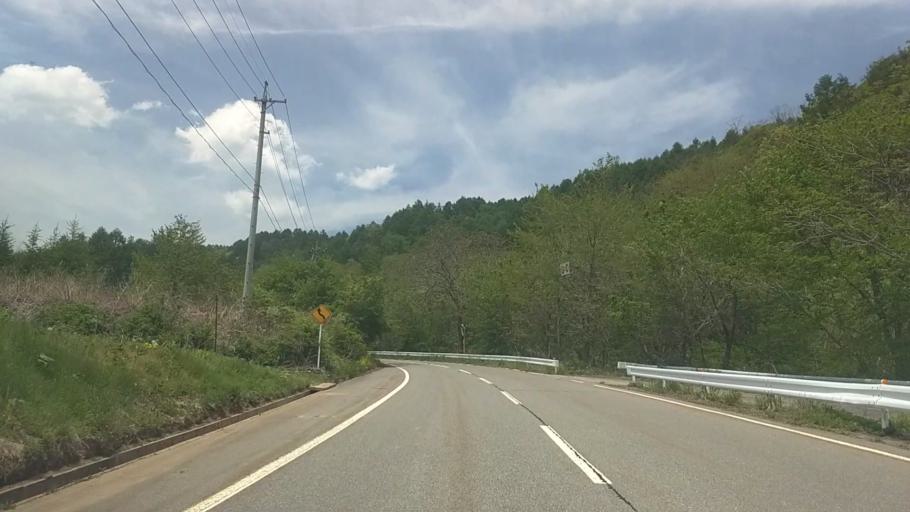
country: JP
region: Nagano
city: Saku
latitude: 36.1057
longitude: 138.4140
